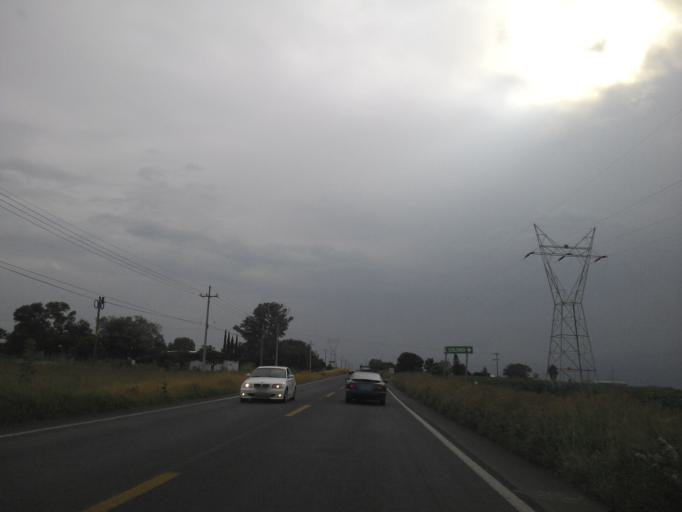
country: MX
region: Jalisco
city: Acatic
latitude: 20.7057
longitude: -102.9617
